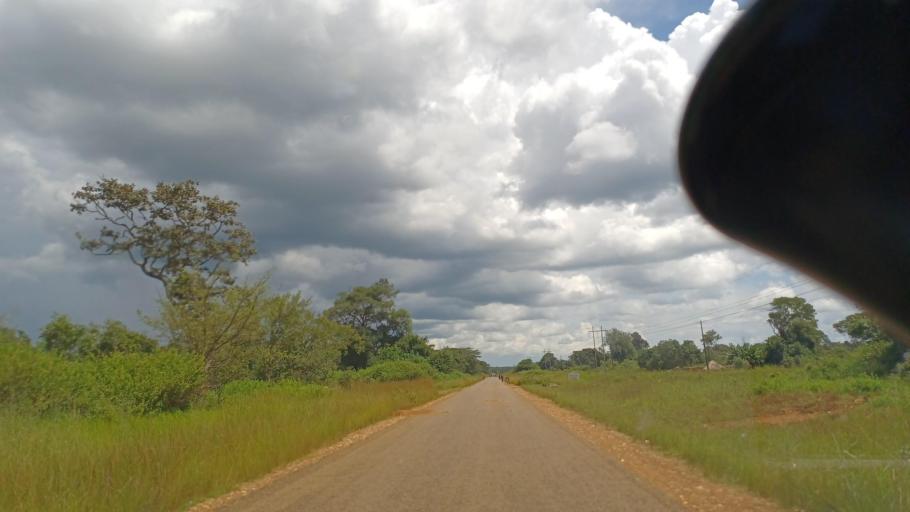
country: ZM
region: North-Western
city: Solwezi
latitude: -12.7639
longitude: 26.0195
